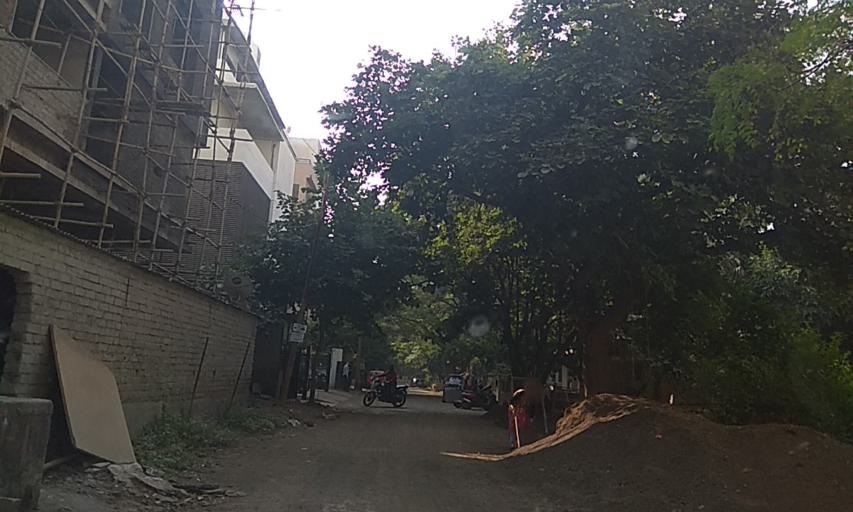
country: IN
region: Maharashtra
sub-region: Pune Division
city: Pimpri
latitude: 18.5627
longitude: 73.7771
